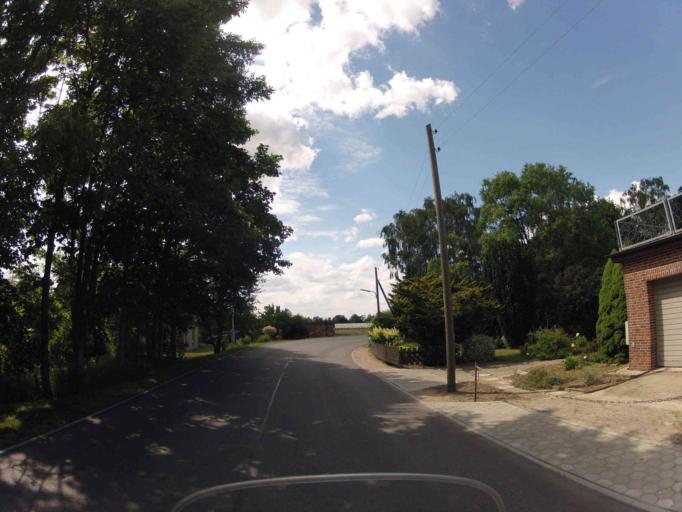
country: DE
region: Lower Saxony
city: Stelle
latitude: 53.4568
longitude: 10.1405
